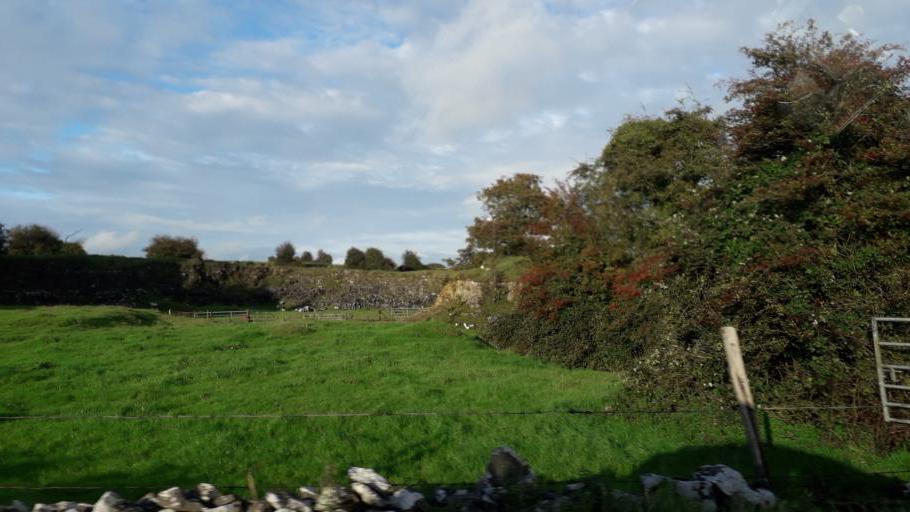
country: IE
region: Connaught
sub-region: Roscommon
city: Roscommon
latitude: 53.7721
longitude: -8.2279
